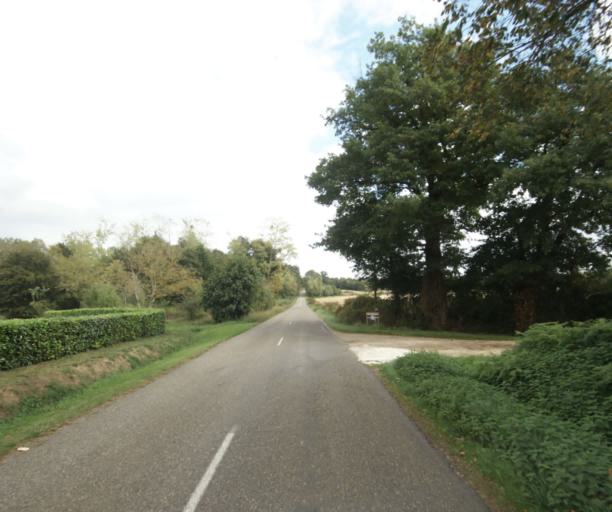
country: FR
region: Midi-Pyrenees
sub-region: Departement du Gers
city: Eauze
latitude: 43.8639
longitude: 0.0109
